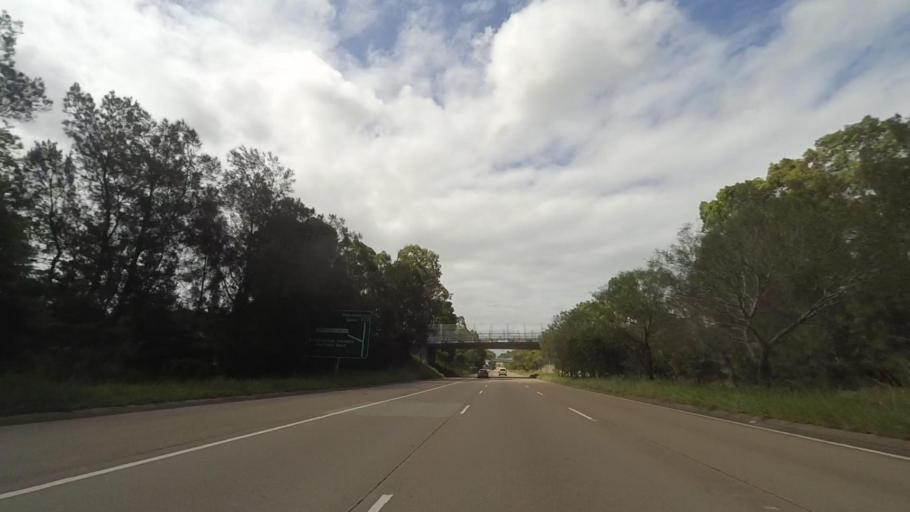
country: AU
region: New South Wales
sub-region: Newcastle
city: North Lambton
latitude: -32.9020
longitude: 151.6936
